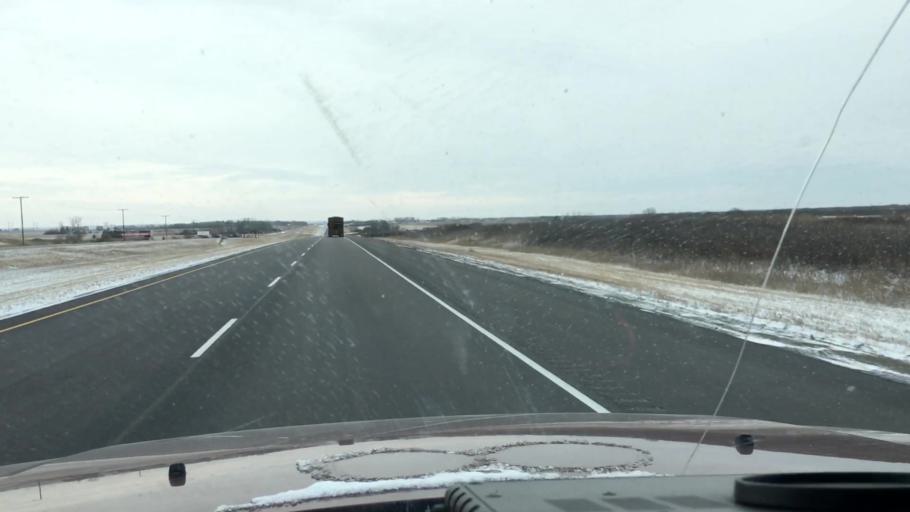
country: CA
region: Saskatchewan
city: Saskatoon
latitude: 51.9278
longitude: -106.5343
